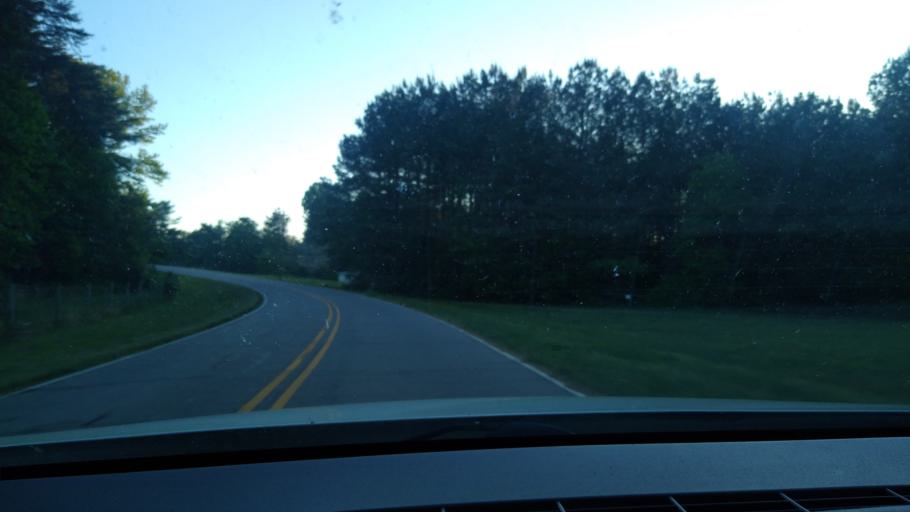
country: US
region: North Carolina
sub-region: Rockingham County
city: Reidsville
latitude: 36.3592
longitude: -79.5652
